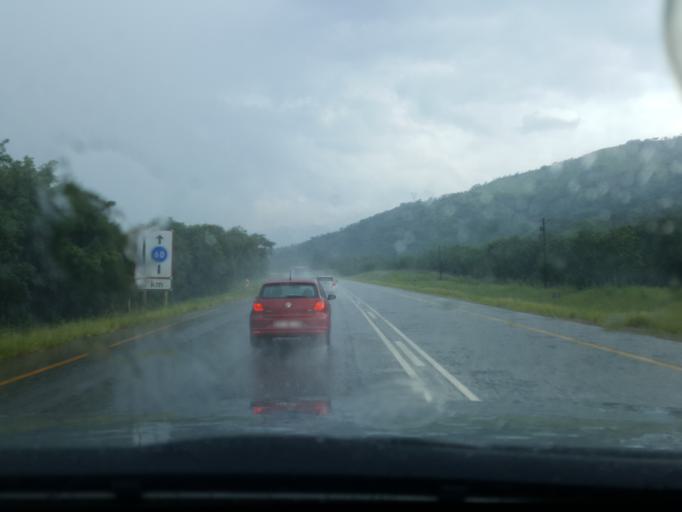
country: ZA
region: Mpumalanga
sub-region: Nkangala District Municipality
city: Belfast
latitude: -25.6018
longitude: 30.4595
